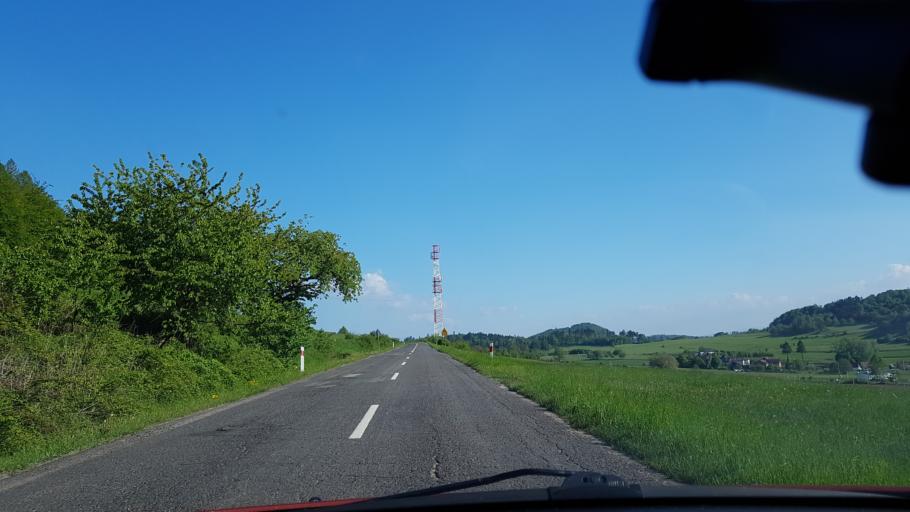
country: PL
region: Lower Silesian Voivodeship
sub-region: Powiat klodzki
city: Bozkow
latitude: 50.5830
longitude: 16.5849
